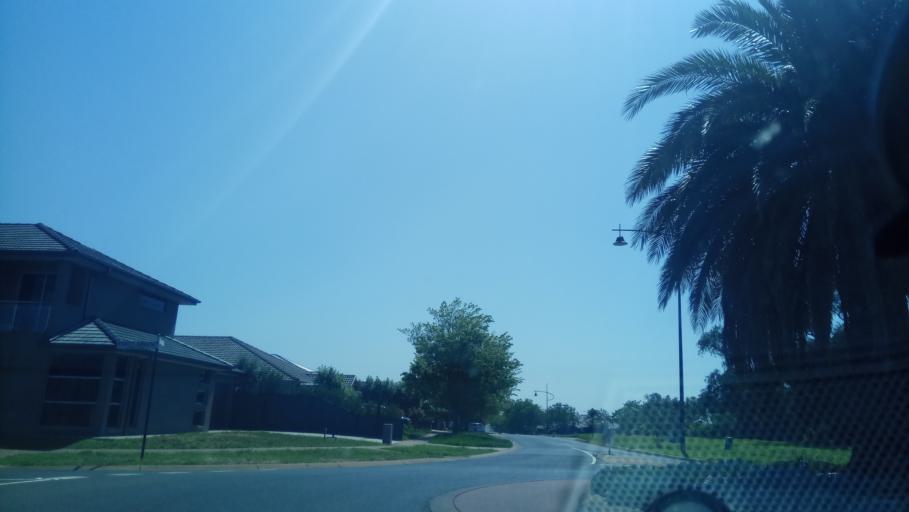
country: AU
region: Victoria
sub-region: Wyndham
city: Point Cook
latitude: -37.8972
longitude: 144.7334
